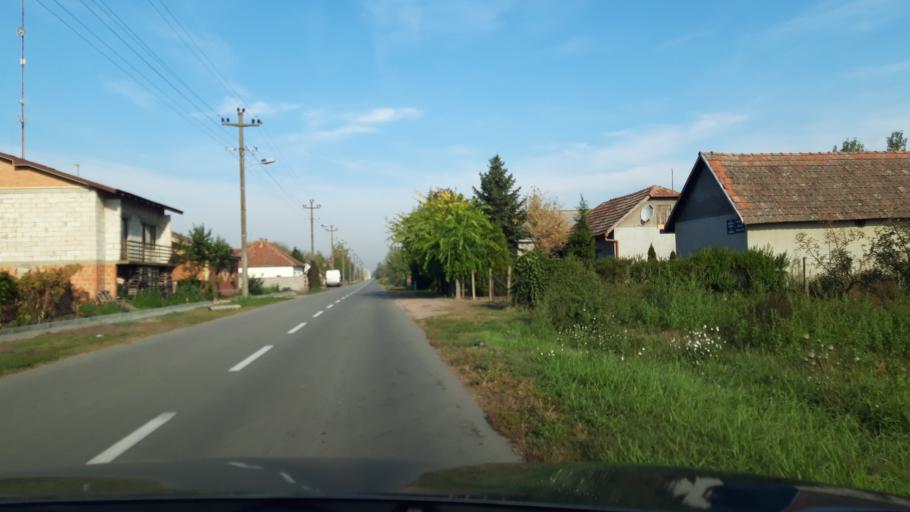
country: HU
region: Csongrad
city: Morahalom
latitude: 46.1301
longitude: 19.8558
